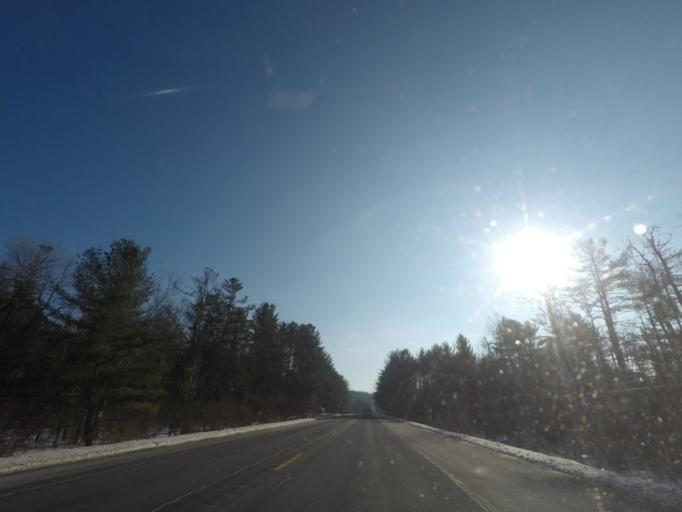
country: US
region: Massachusetts
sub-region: Berkshire County
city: Lanesborough
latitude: 42.5226
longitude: -73.3579
